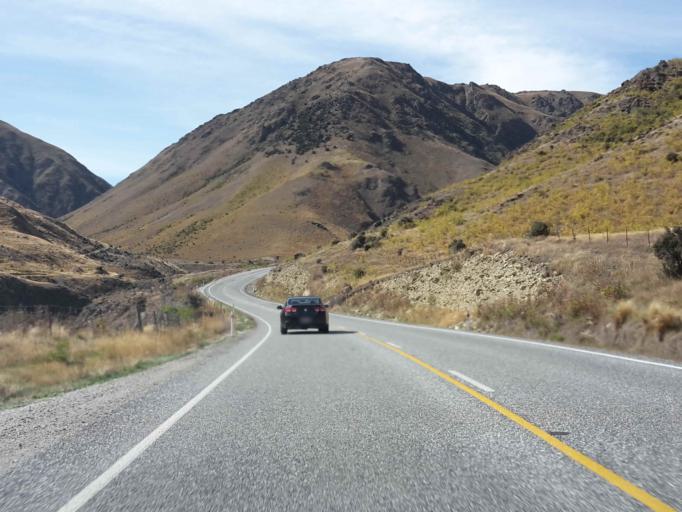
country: NZ
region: Otago
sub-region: Queenstown-Lakes District
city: Wanaka
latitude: -44.6107
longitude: 169.5350
